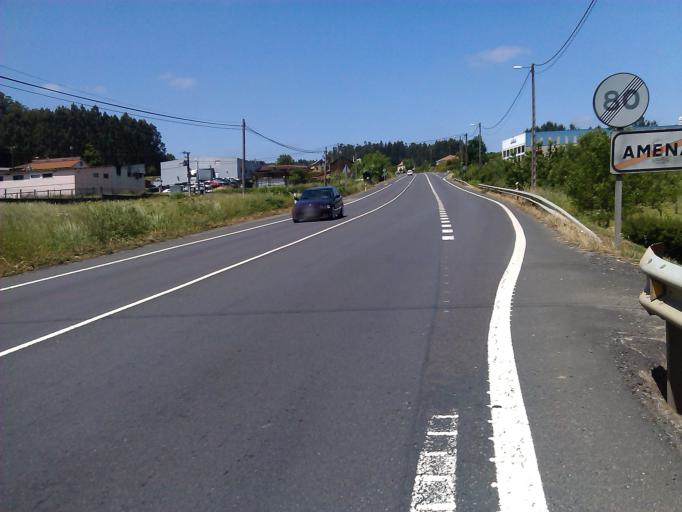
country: ES
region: Galicia
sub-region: Provincia da Coruna
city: Oroso
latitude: 42.9073
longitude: -8.3951
